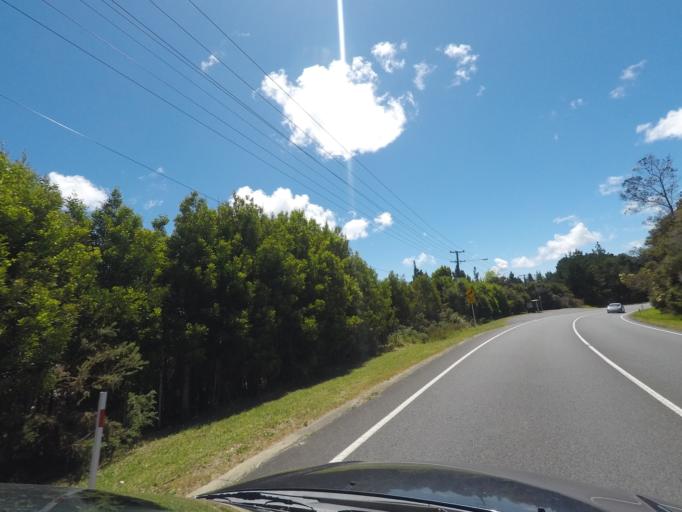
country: NZ
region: Auckland
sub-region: Auckland
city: Rothesay Bay
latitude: -36.7525
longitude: 174.6663
